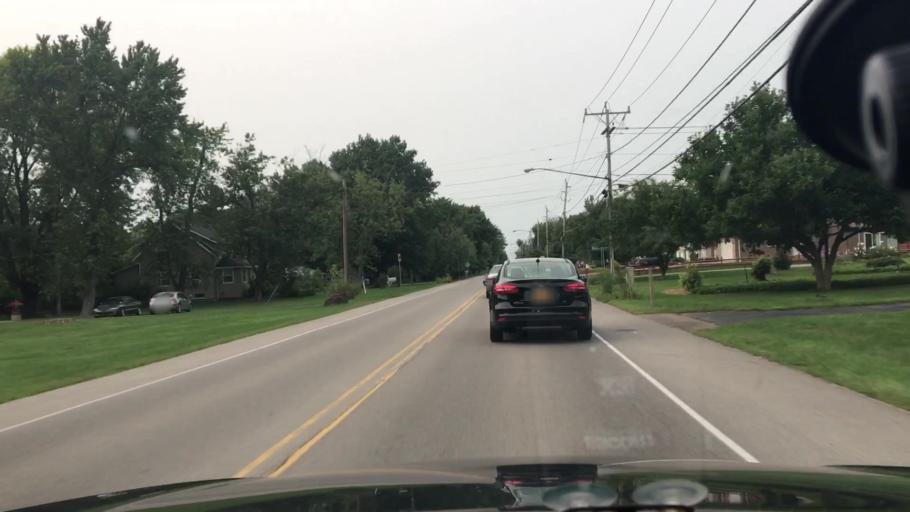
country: US
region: New York
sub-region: Erie County
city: Blasdell
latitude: 42.7547
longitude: -78.7951
